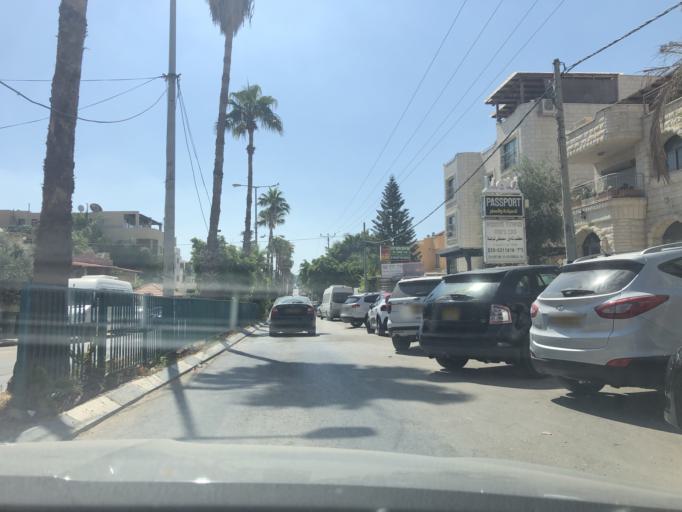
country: IL
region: Central District
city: Jaljulya
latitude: 32.1538
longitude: 34.9517
